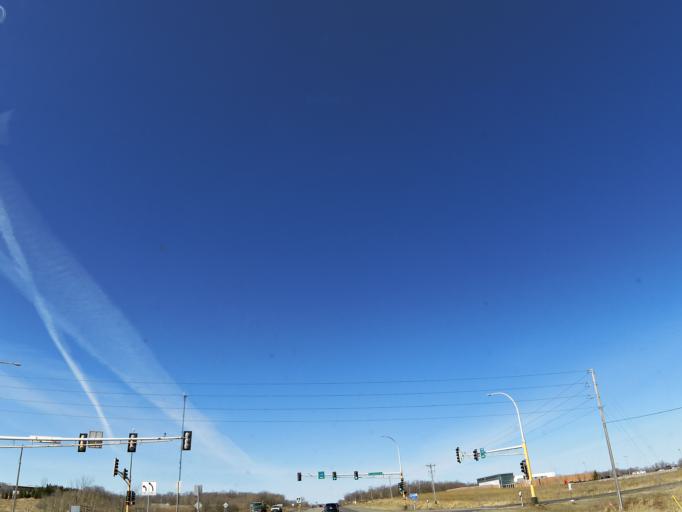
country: US
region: Minnesota
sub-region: Hennepin County
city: Medina
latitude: 45.0514
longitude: -93.5627
